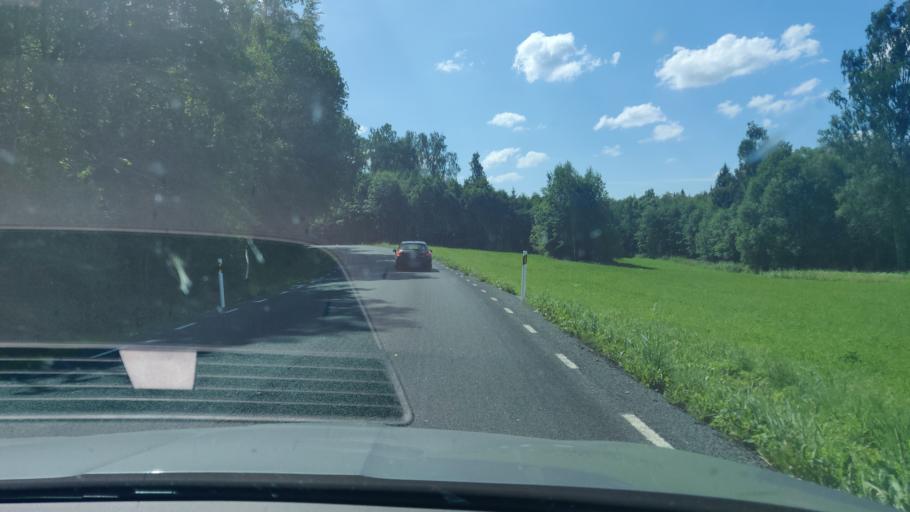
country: EE
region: Tartu
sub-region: Elva linn
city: Elva
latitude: 58.1558
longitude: 26.4701
